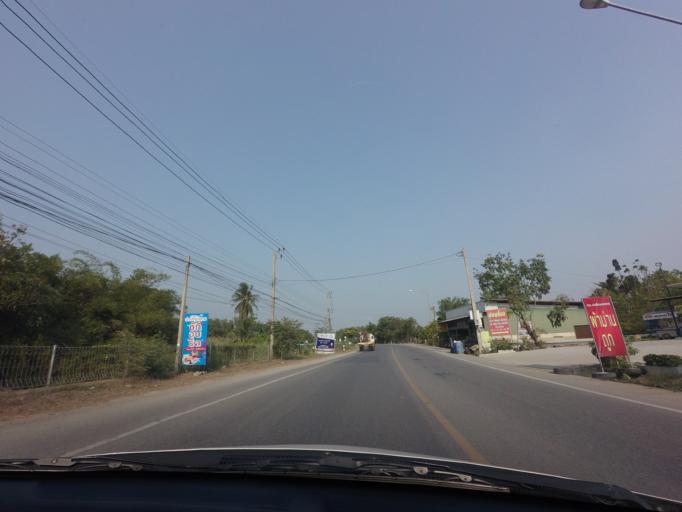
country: TH
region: Nonthaburi
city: Bang Yai
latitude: 13.8085
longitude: 100.3653
